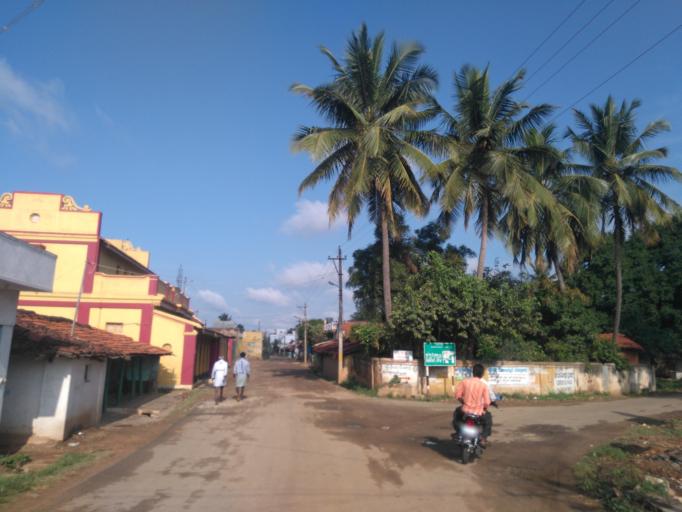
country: IN
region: Karnataka
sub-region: Mysore
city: Tirumakudal Narsipur
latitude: 12.2579
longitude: 77.0112
